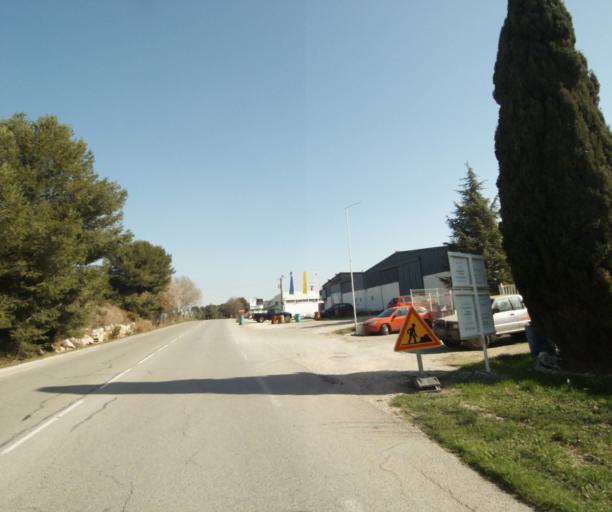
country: FR
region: Provence-Alpes-Cote d'Azur
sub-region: Departement des Bouches-du-Rhone
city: Simiane-Collongue
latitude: 43.4490
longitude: 5.4445
